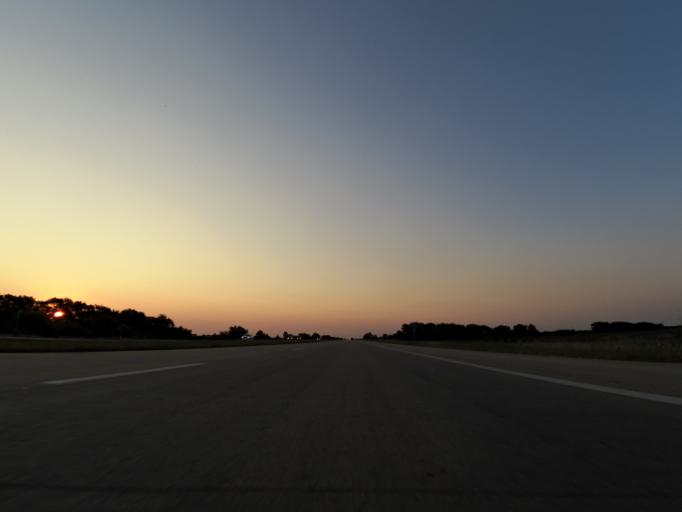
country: US
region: Kansas
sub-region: Reno County
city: South Hutchinson
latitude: 37.9612
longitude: -97.9144
